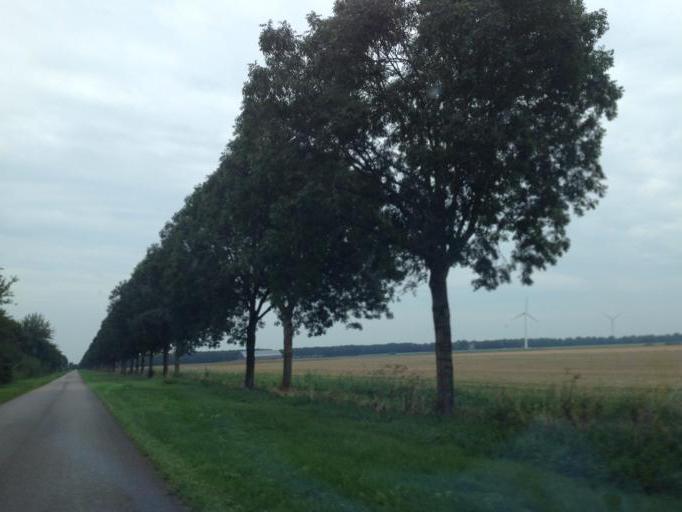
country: NL
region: Flevoland
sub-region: Gemeente Lelystad
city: Lelystad
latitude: 52.4268
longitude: 5.4243
